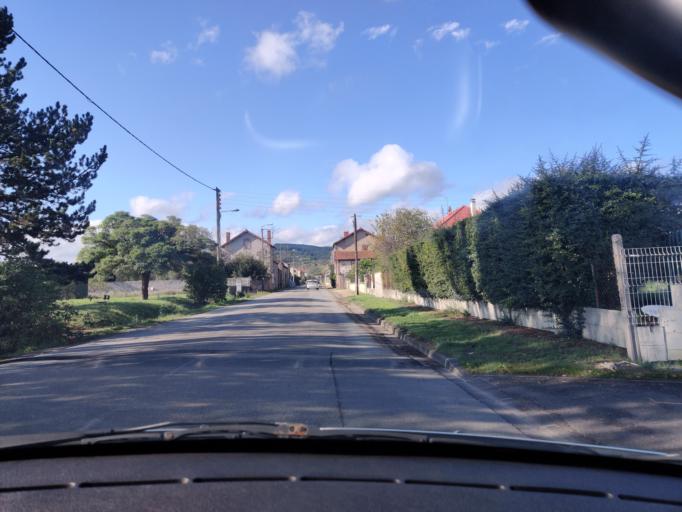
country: FR
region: Auvergne
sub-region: Departement du Puy-de-Dome
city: Combronde
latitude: 45.9836
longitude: 3.0977
